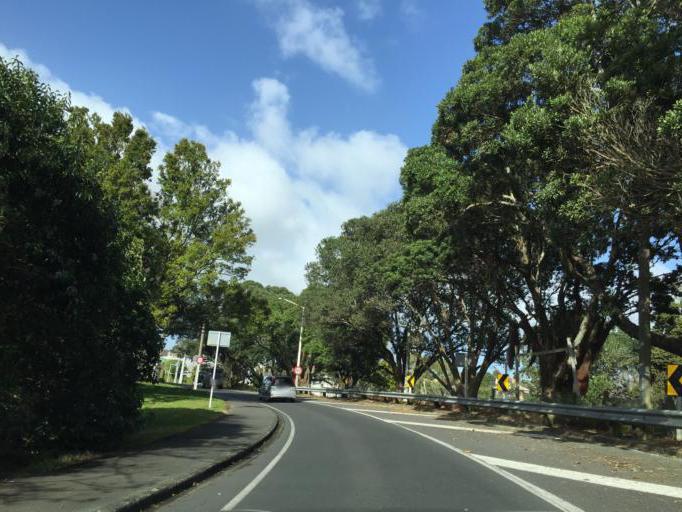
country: NZ
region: Auckland
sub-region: Auckland
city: Auckland
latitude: -36.8394
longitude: 174.7416
